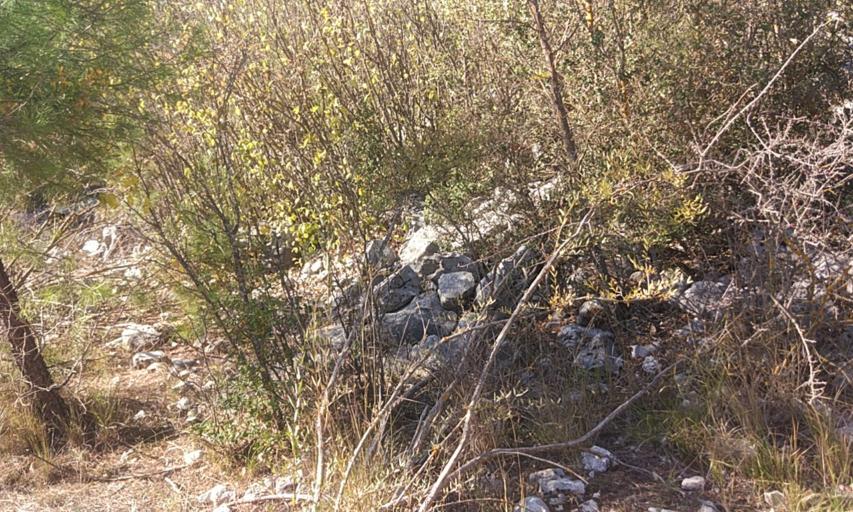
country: TR
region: Antalya
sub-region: Kemer
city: Goeynuek
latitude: 36.6355
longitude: 30.4473
